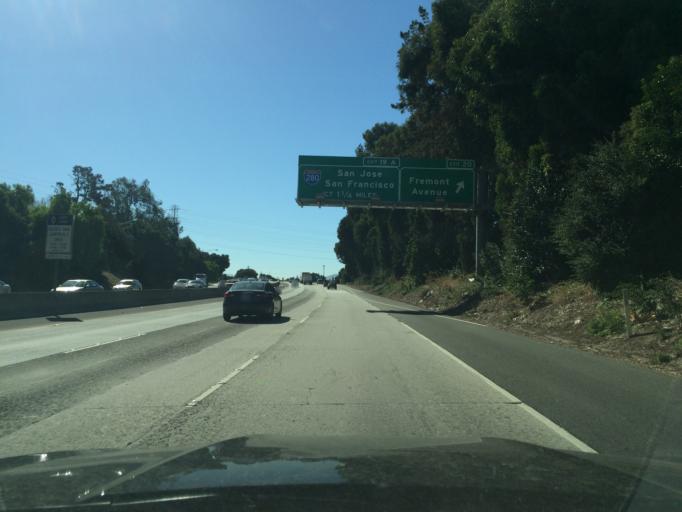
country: US
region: California
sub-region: Santa Clara County
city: Sunnyvale
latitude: 37.3565
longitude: -122.0626
